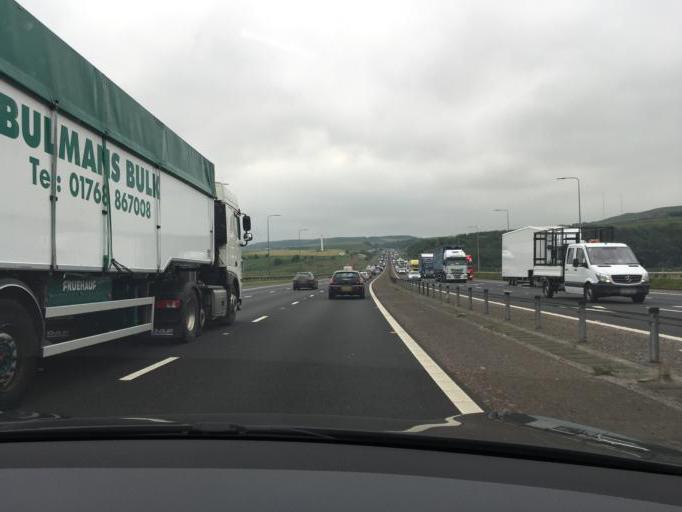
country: GB
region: England
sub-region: Calderdale
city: Ripponden
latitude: 53.6476
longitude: -1.9269
